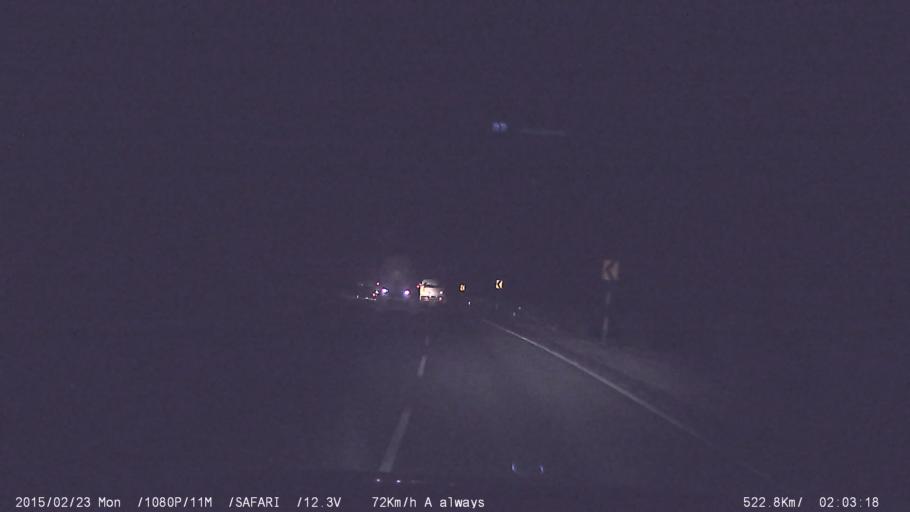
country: IN
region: Tamil Nadu
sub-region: Krishnagiri
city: Krishnagiri
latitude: 12.6435
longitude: 78.0551
